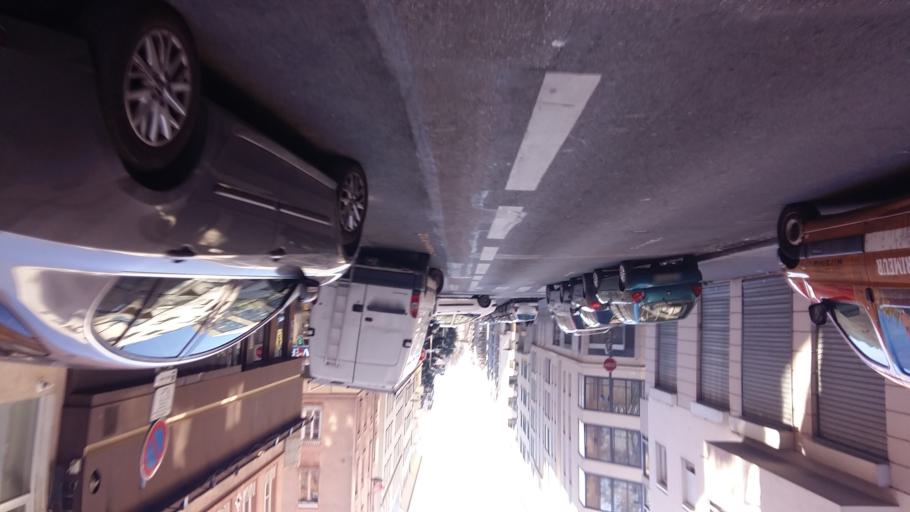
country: FR
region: Rhone-Alpes
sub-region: Departement du Rhone
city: Lyon
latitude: 45.7572
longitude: 4.8495
